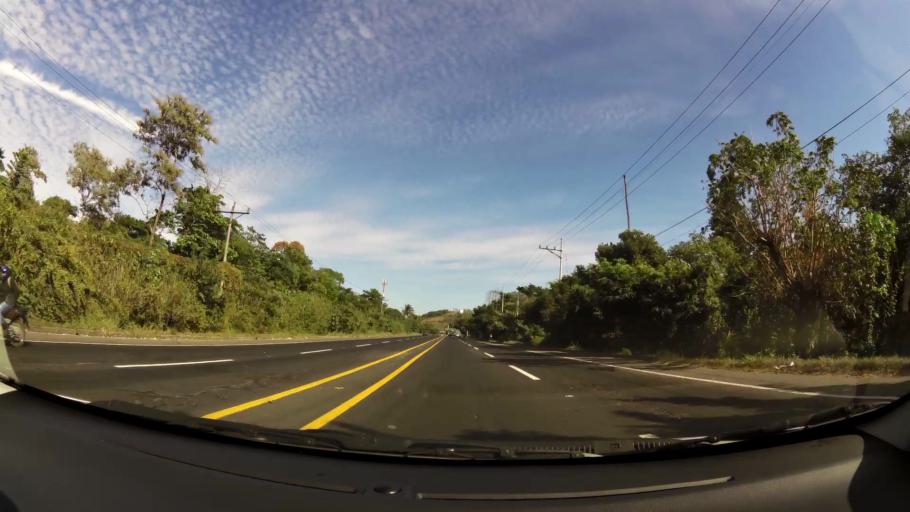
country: SV
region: Santa Ana
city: Santa Ana
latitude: 13.9855
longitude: -89.6019
